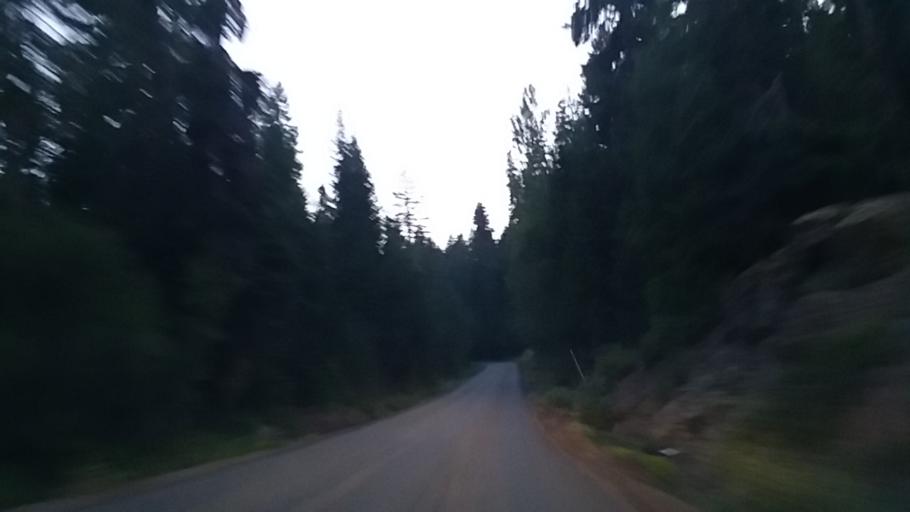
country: US
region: Washington
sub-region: Kittitas County
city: Cle Elum
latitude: 47.3382
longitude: -121.2550
